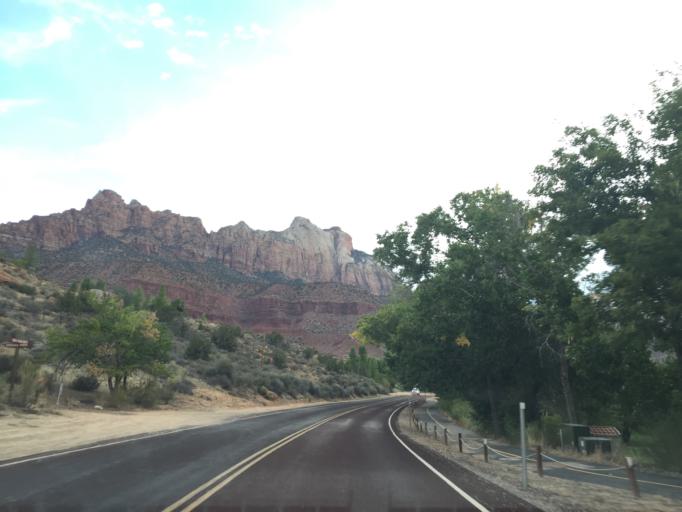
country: US
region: Utah
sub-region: Washington County
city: Hildale
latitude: 37.1710
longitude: -113.0135
